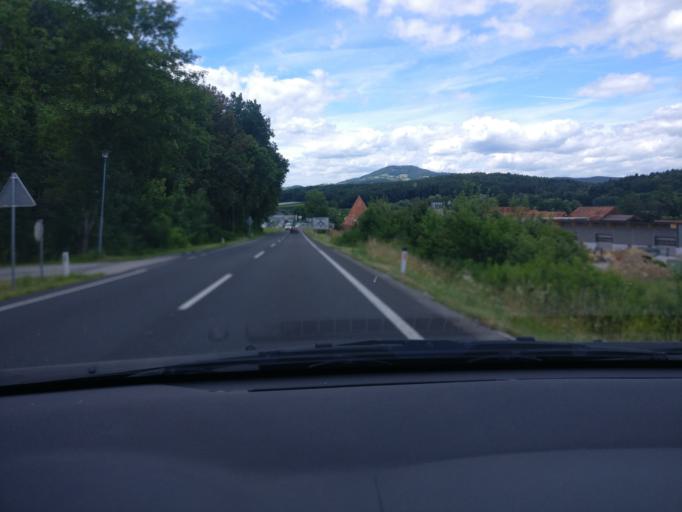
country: AT
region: Styria
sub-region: Politischer Bezirk Weiz
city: Oberrettenbach
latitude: 47.1467
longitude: 15.7709
